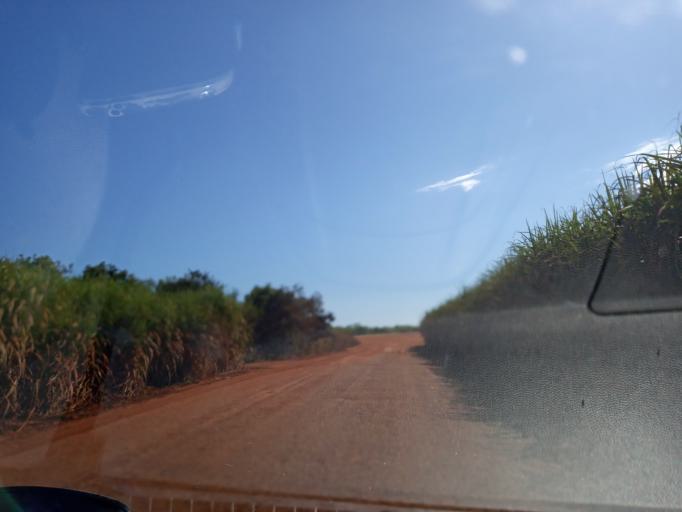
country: BR
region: Goias
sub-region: Itumbiara
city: Itumbiara
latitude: -18.4453
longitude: -49.1755
